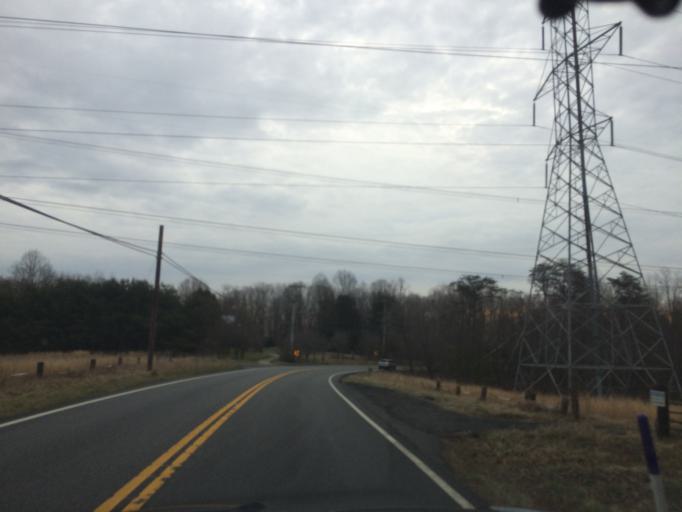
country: US
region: Maryland
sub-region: Montgomery County
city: Ashton-Sandy Spring
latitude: 39.1611
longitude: -76.9844
